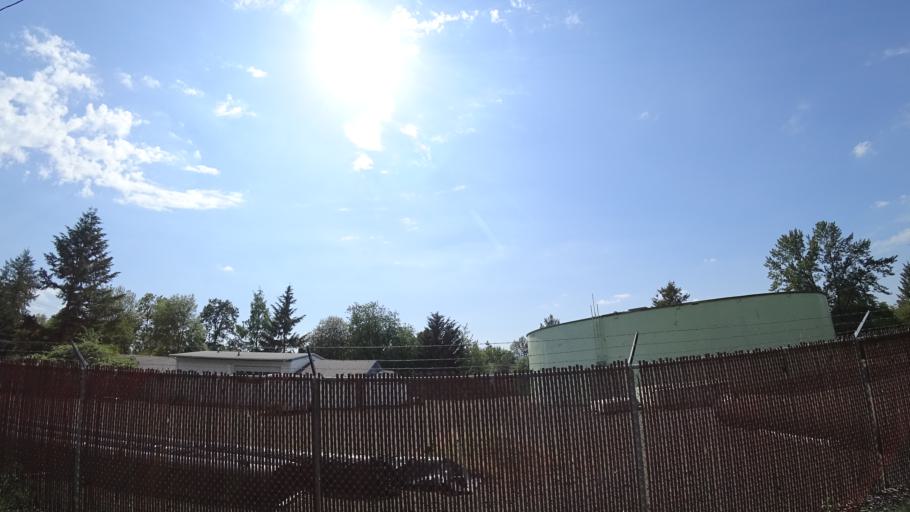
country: US
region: Oregon
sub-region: Washington County
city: Garden Home-Whitford
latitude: 45.4554
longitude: -122.7436
